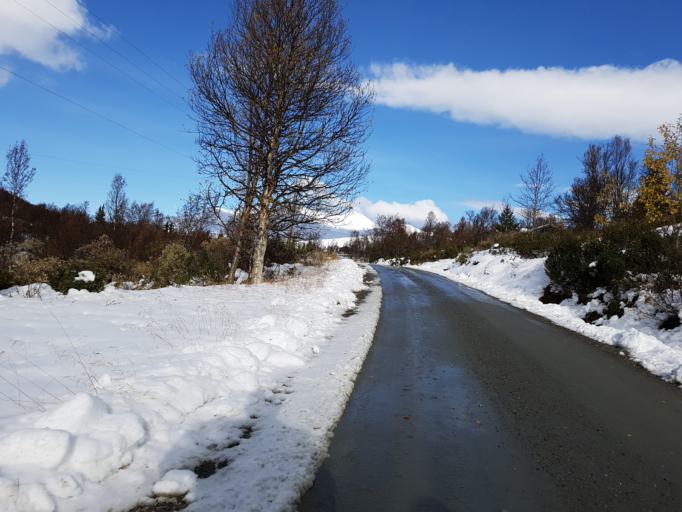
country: NO
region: Oppland
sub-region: Sel
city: Otta
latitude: 61.8196
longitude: 9.6780
